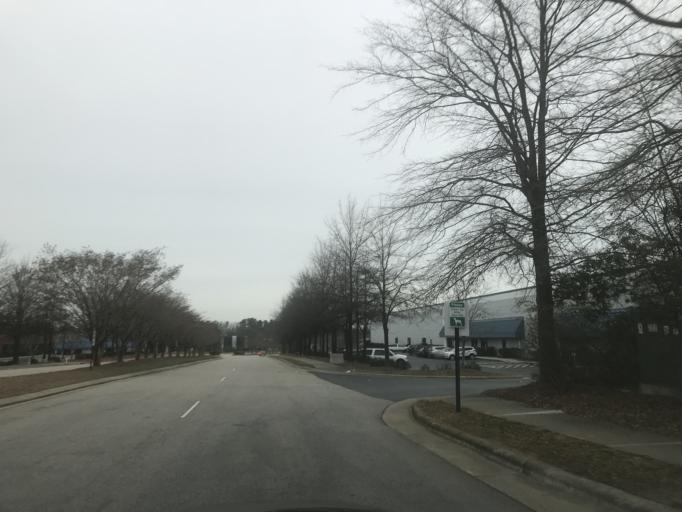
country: US
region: North Carolina
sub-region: Wake County
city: Raleigh
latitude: 35.8716
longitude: -78.5898
